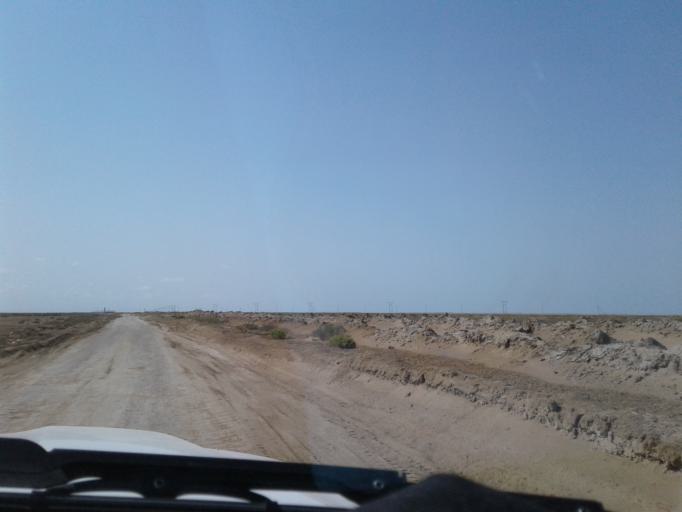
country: IR
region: Golestan
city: Gomishan
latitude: 37.8295
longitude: 53.9215
